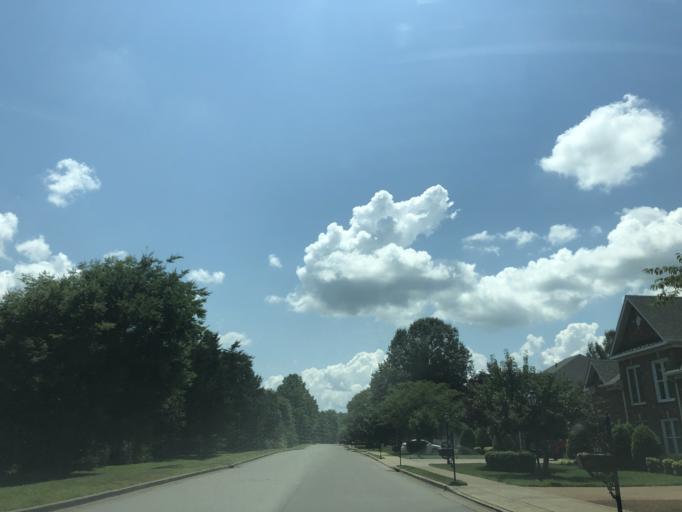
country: US
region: Tennessee
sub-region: Davidson County
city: Lakewood
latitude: 36.1947
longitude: -86.6037
